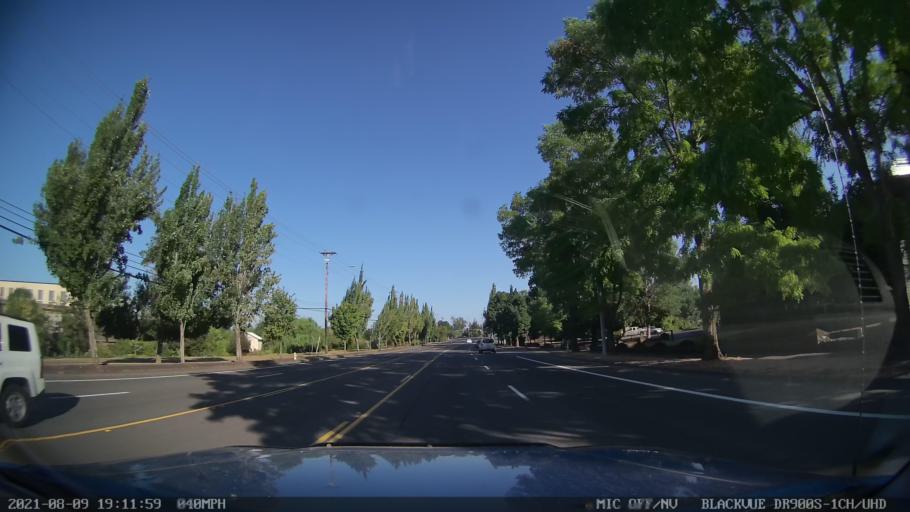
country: US
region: Oregon
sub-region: Marion County
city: Four Corners
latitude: 44.9311
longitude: -123.0070
